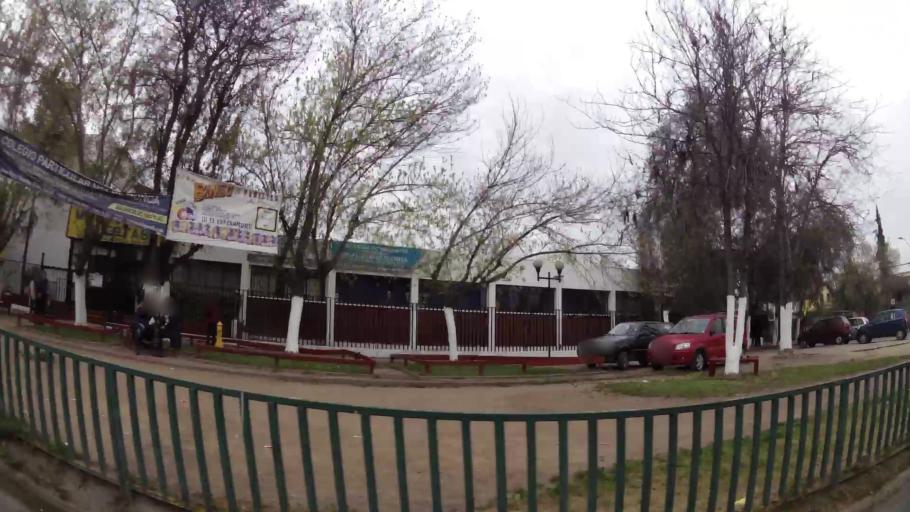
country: CL
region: Santiago Metropolitan
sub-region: Provincia de Santiago
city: Villa Presidente Frei, Nunoa, Santiago, Chile
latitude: -33.4706
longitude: -70.5895
